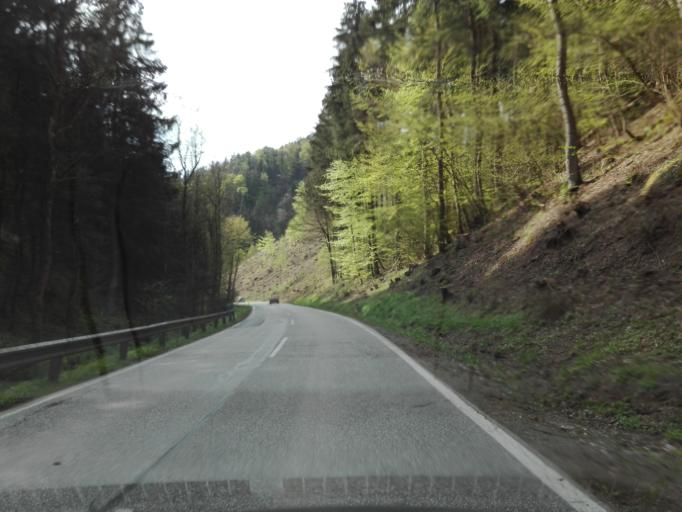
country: AT
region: Upper Austria
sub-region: Politischer Bezirk Urfahr-Umgebung
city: Feldkirchen an der Donau
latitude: 48.3833
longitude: 14.0736
